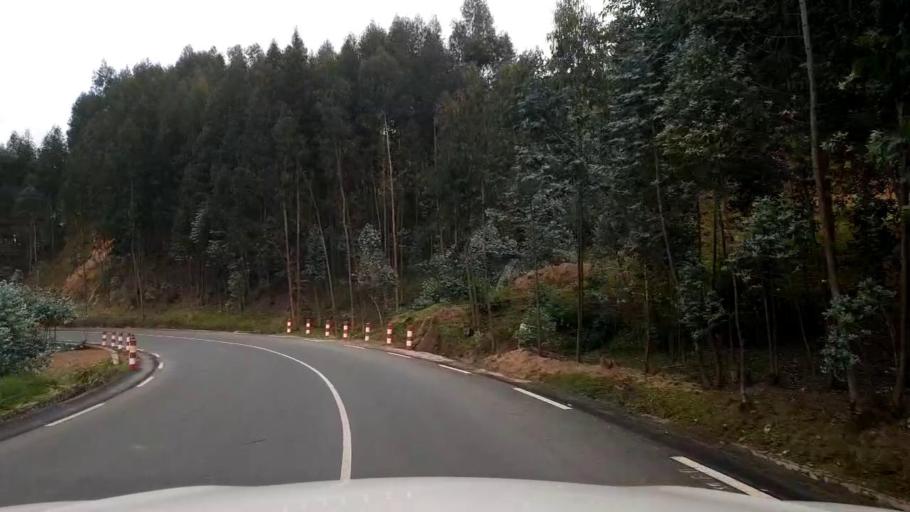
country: RW
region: Northern Province
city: Musanze
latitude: -1.6872
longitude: 29.5218
